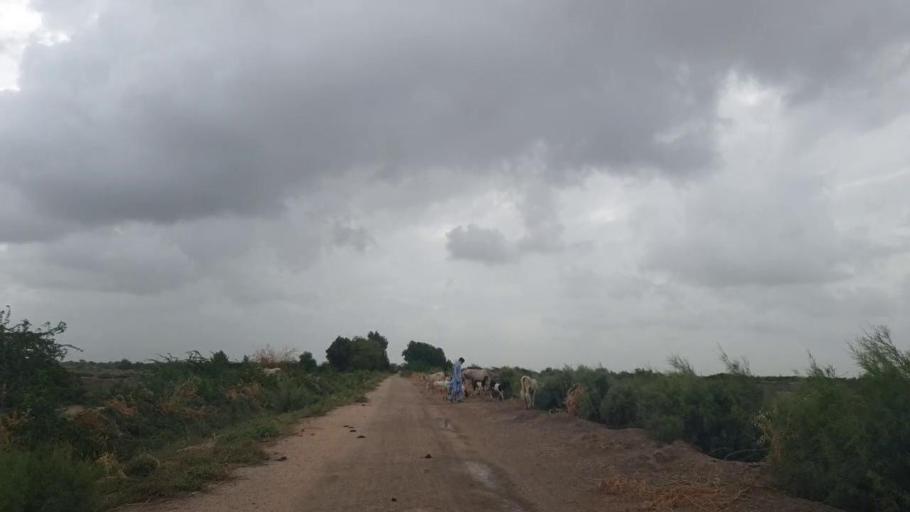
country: PK
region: Sindh
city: Tando Bago
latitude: 24.8481
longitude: 69.1616
